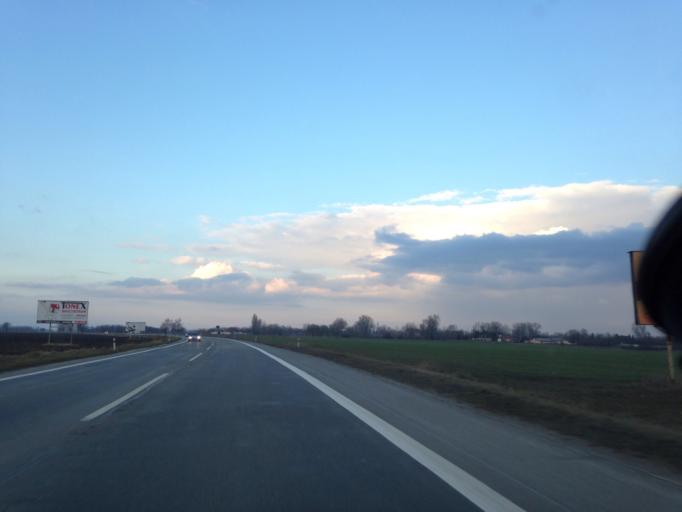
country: SK
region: Nitriansky
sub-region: Okres Komarno
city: Hurbanovo
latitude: 47.8027
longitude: 18.1856
